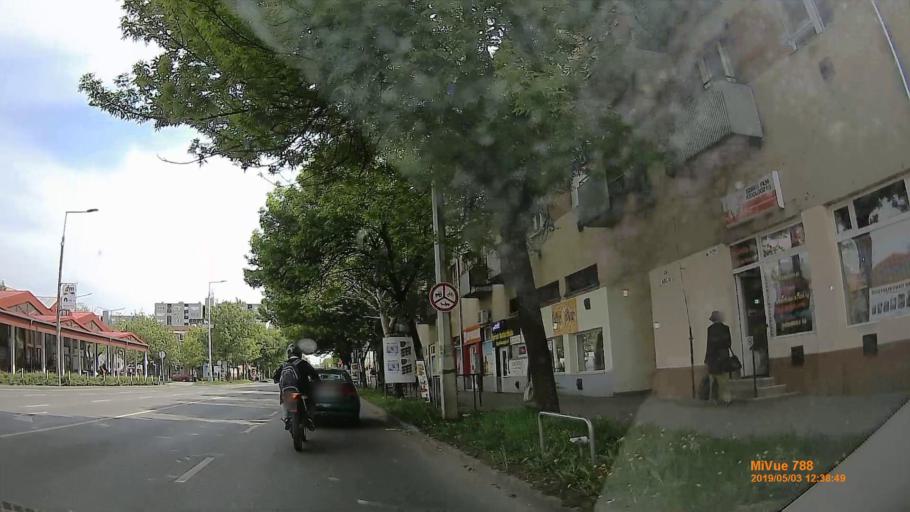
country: HU
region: Jasz-Nagykun-Szolnok
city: Szolnok
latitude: 47.1770
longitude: 20.1954
